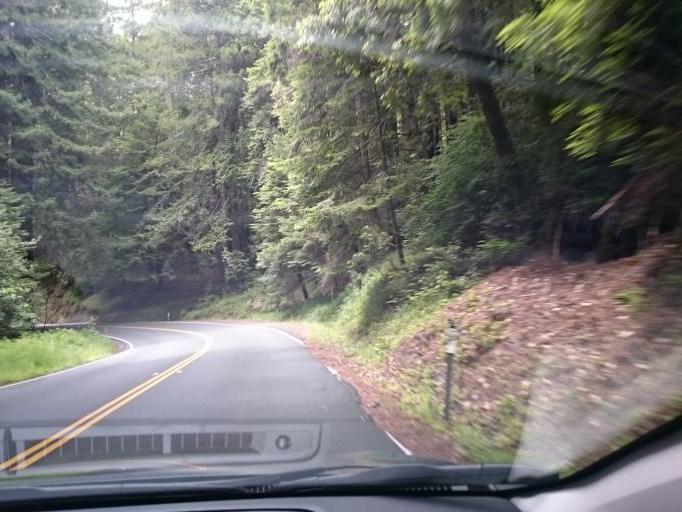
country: US
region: California
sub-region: Mendocino County
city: Fort Bragg
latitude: 39.1803
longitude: -123.6969
